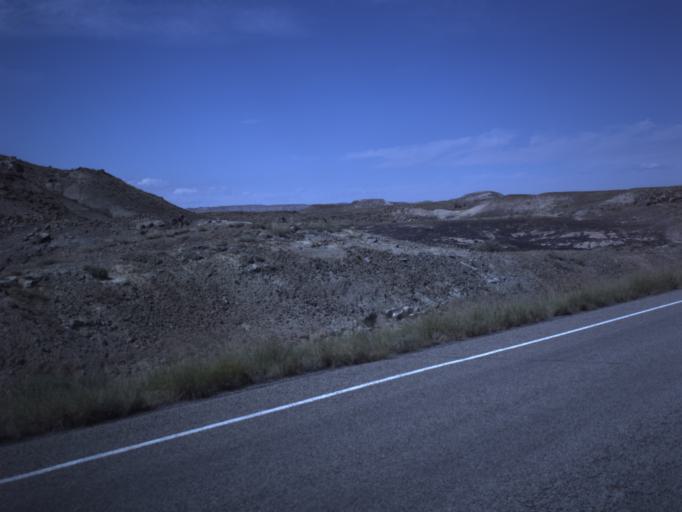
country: US
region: Colorado
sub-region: Montezuma County
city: Towaoc
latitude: 37.1514
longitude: -109.0471
